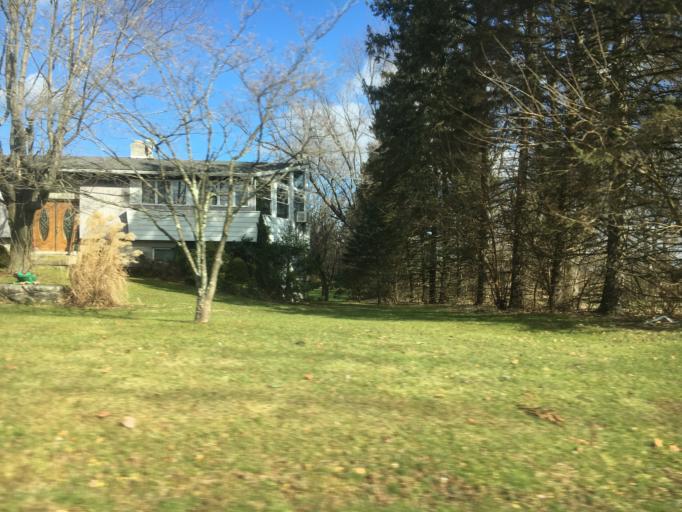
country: US
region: Pennsylvania
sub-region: Lehigh County
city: Egypt
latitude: 40.6836
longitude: -75.5425
